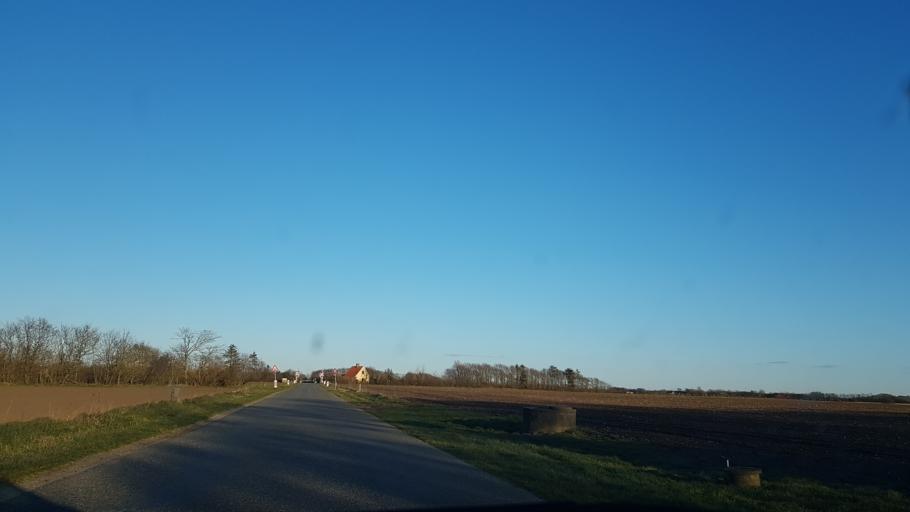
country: DK
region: South Denmark
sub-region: Esbjerg Kommune
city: Ribe
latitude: 55.3849
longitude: 8.7427
